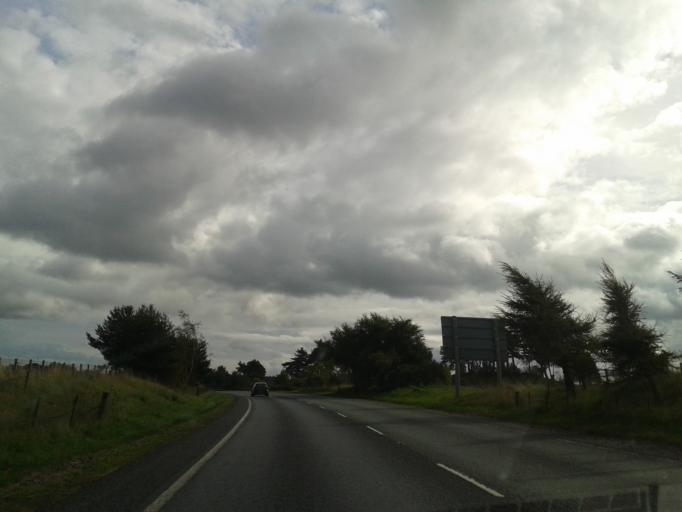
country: GB
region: Scotland
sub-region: Moray
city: Lhanbryd
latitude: 57.6350
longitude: -3.2314
